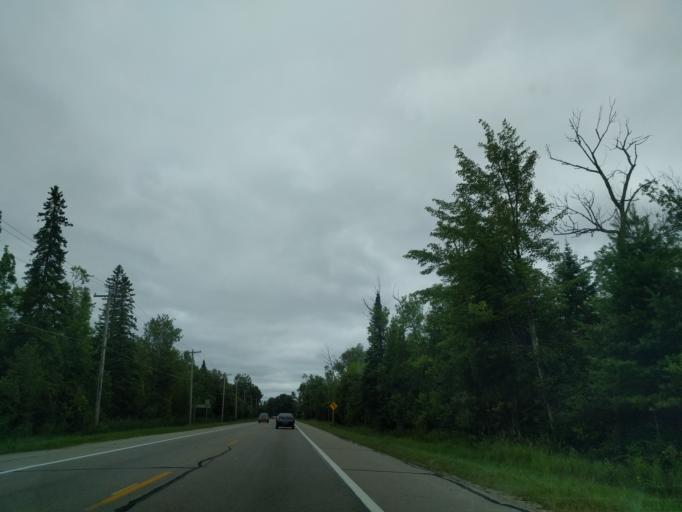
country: US
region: Michigan
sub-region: Delta County
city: Escanaba
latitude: 45.7013
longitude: -87.1012
